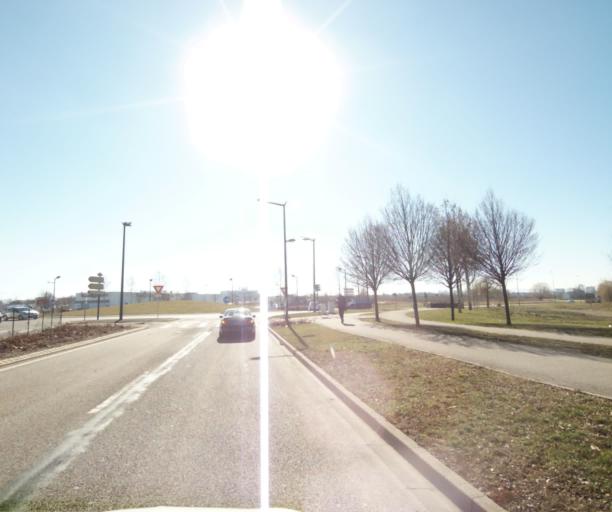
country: FR
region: Lorraine
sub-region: Departement de Meurthe-et-Moselle
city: Pulnoy
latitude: 48.7088
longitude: 6.2439
